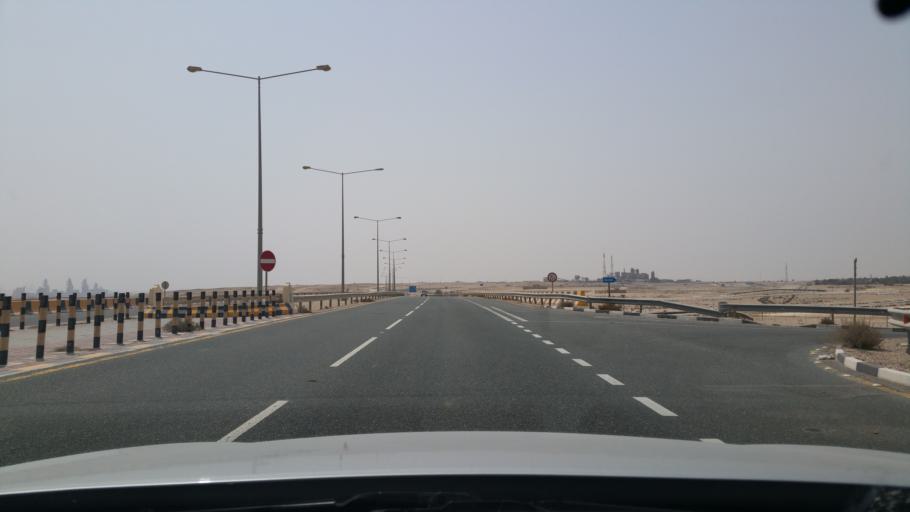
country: QA
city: Umm Bab
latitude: 25.2273
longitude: 50.8039
